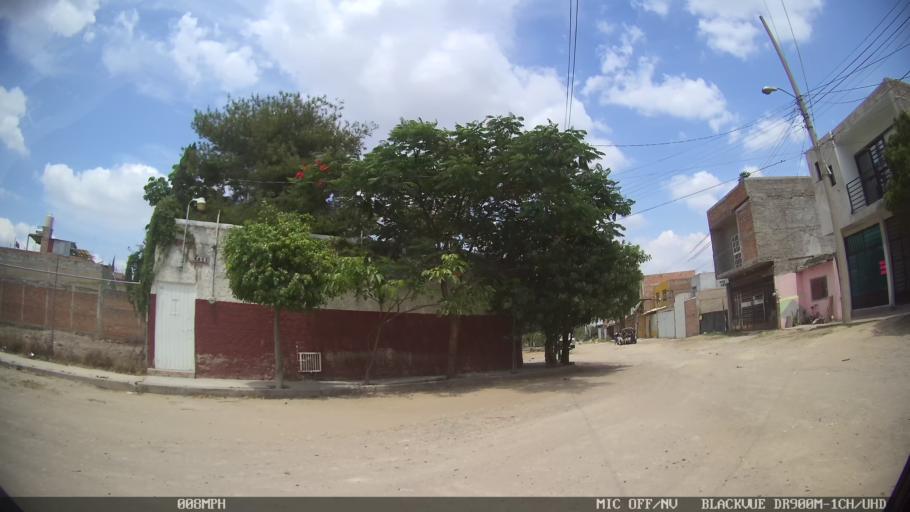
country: MX
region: Jalisco
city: Tonala
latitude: 20.6814
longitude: -103.2406
